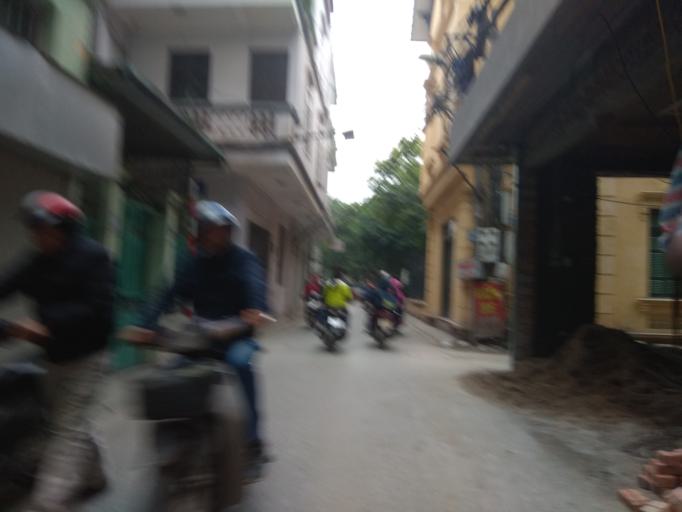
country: VN
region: Ha Noi
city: Hoan Kiem
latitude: 21.0442
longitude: 105.8697
